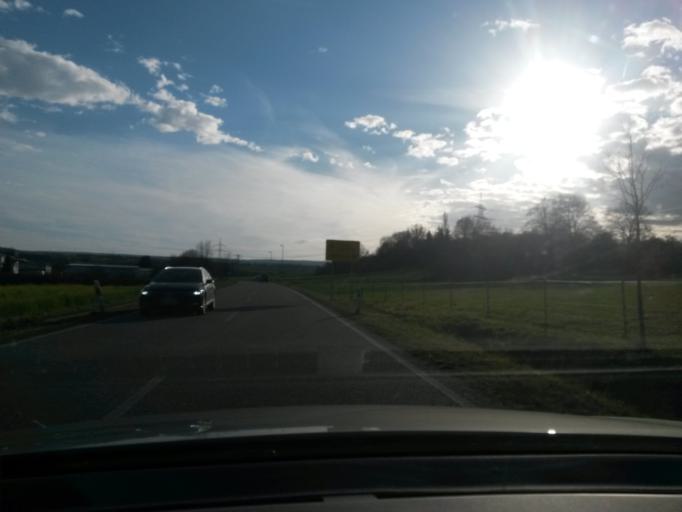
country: DE
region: Baden-Wuerttemberg
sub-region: Karlsruhe Region
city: Konigsbach-Stein
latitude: 48.9132
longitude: 8.5601
